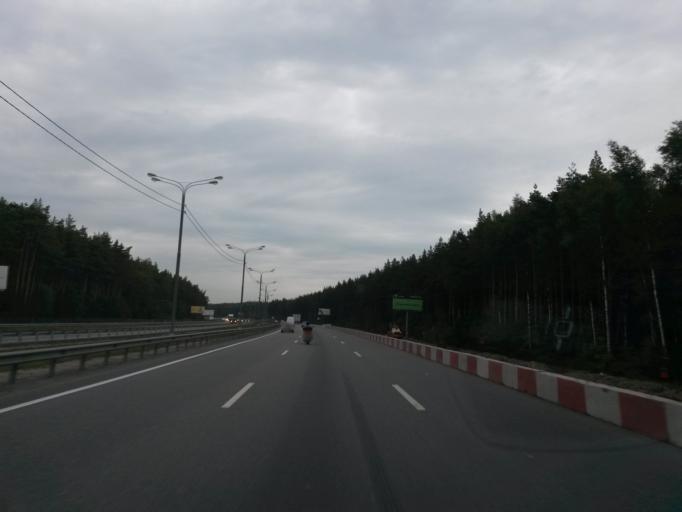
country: RU
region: Moskovskaya
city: Vostryakovo
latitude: 55.4382
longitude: 37.7992
